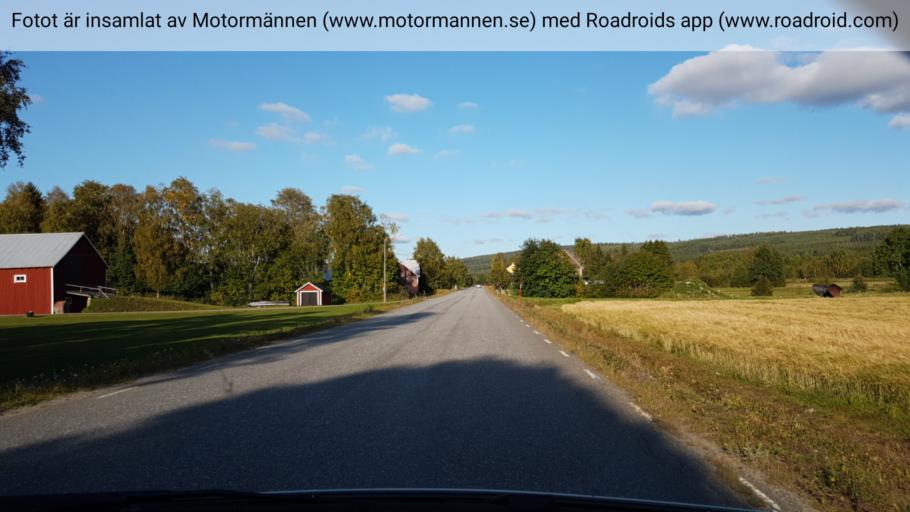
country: SE
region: Vaesterbotten
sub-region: Vannas Kommun
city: Vannasby
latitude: 63.9369
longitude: 19.8626
